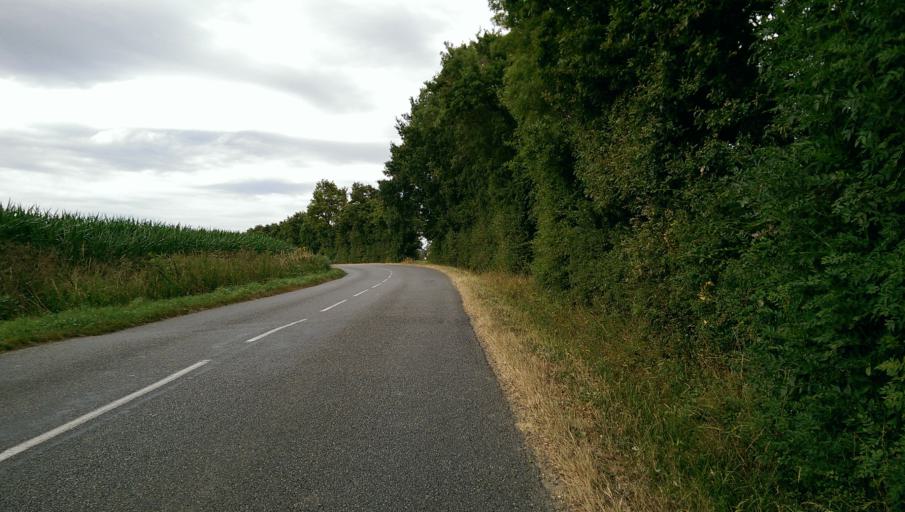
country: FR
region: Pays de la Loire
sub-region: Departement de la Loire-Atlantique
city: Vieillevigne
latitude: 46.9773
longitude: -1.4308
